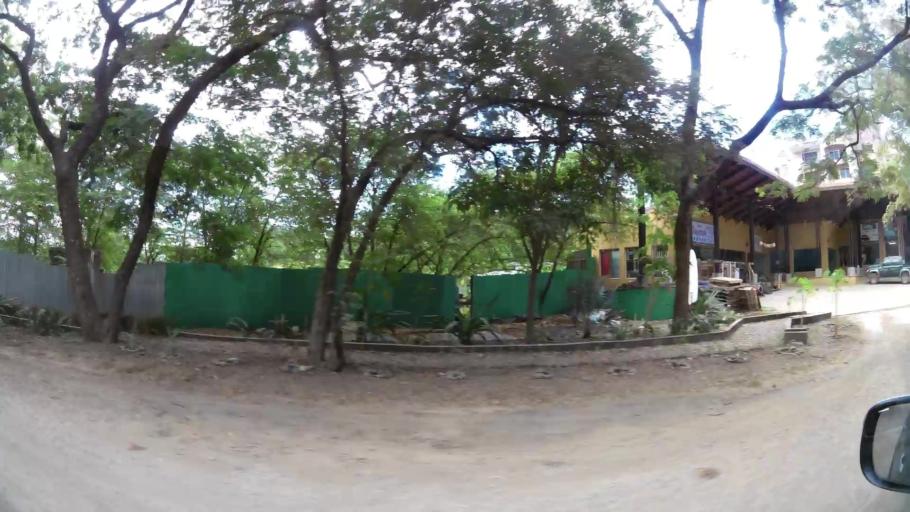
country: CR
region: Guanacaste
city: Santa Cruz
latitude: 10.2916
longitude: -85.8498
